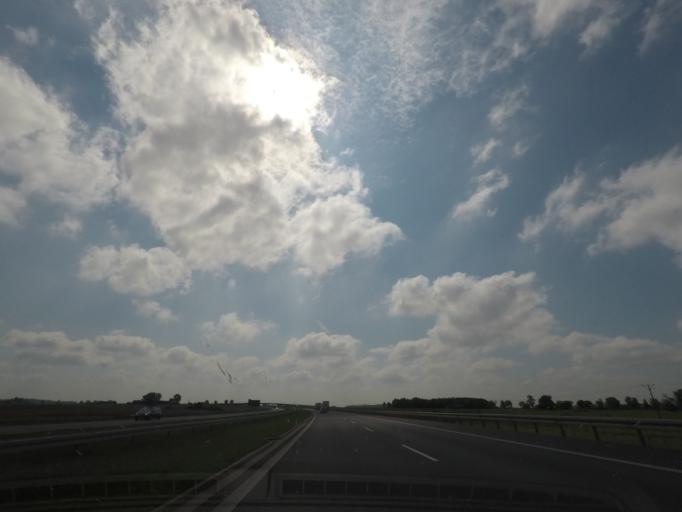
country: PL
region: Kujawsko-Pomorskie
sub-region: Powiat wloclawski
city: Brzesc Kujawski
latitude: 52.6683
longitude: 18.9060
